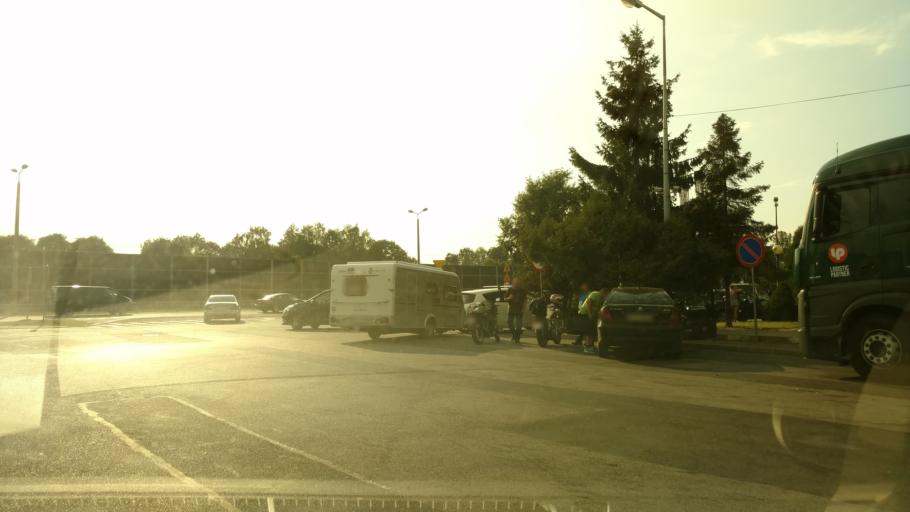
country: PL
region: Silesian Voivodeship
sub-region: Powiat pszczynski
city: Pszczyna
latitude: 49.9875
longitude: 18.9555
